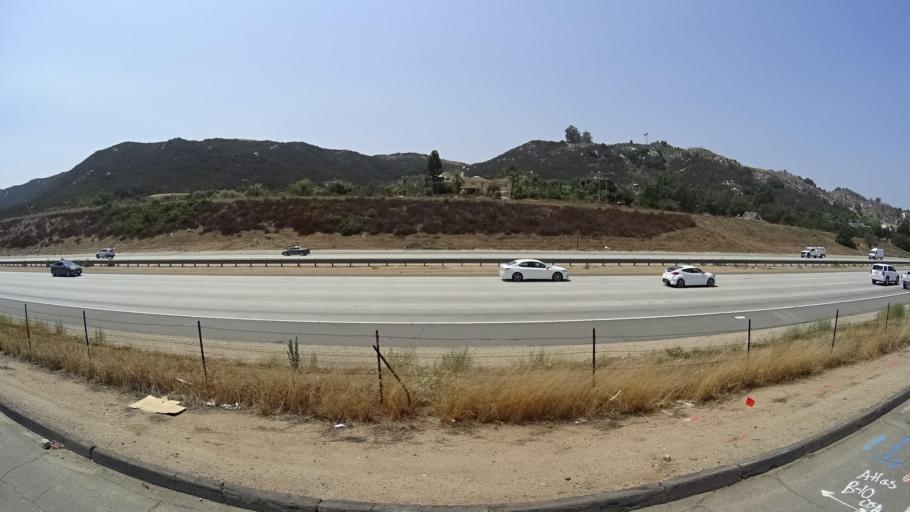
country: US
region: California
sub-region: San Diego County
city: Hidden Meadows
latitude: 33.1830
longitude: -117.1169
